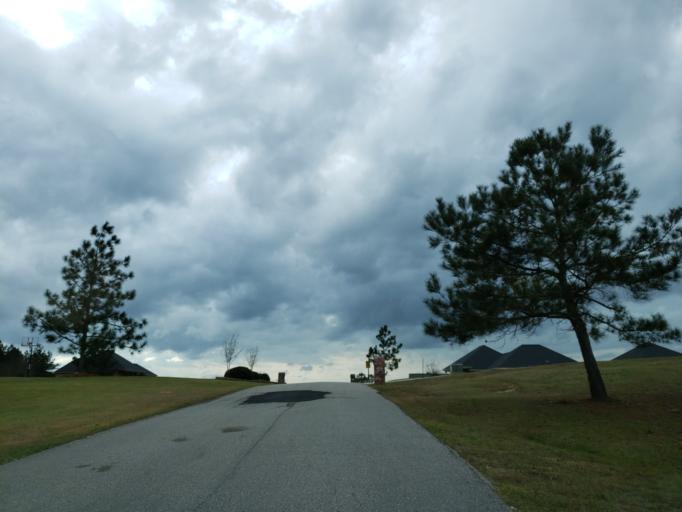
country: US
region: Mississippi
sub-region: Jones County
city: Ellisville
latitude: 31.5513
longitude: -89.2538
